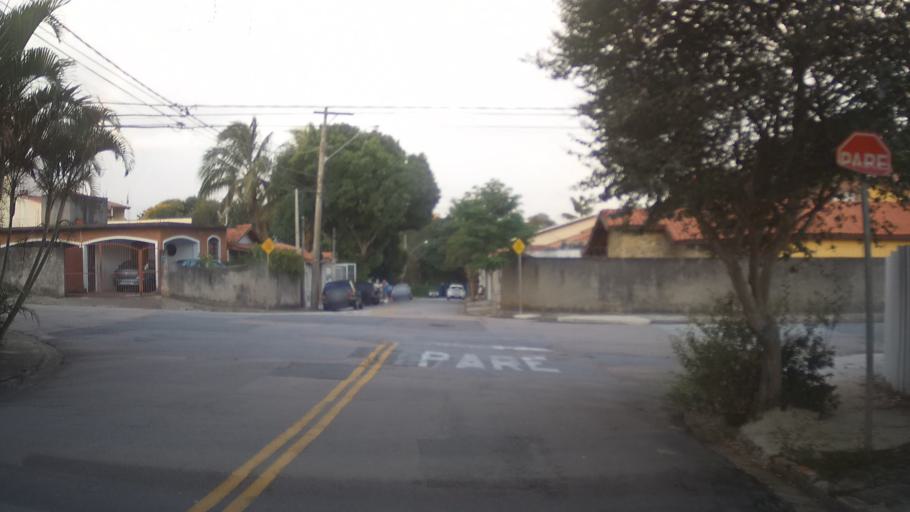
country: BR
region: Sao Paulo
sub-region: Jundiai
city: Jundiai
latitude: -23.1886
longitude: -46.9628
